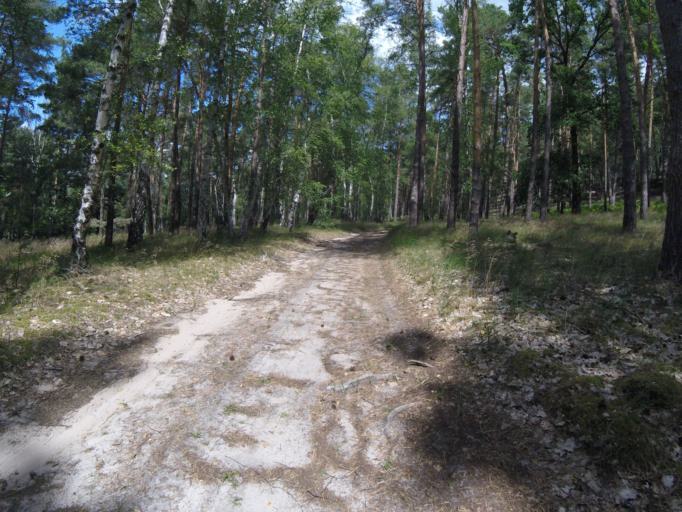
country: DE
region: Brandenburg
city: Bestensee
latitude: 52.2054
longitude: 13.6391
